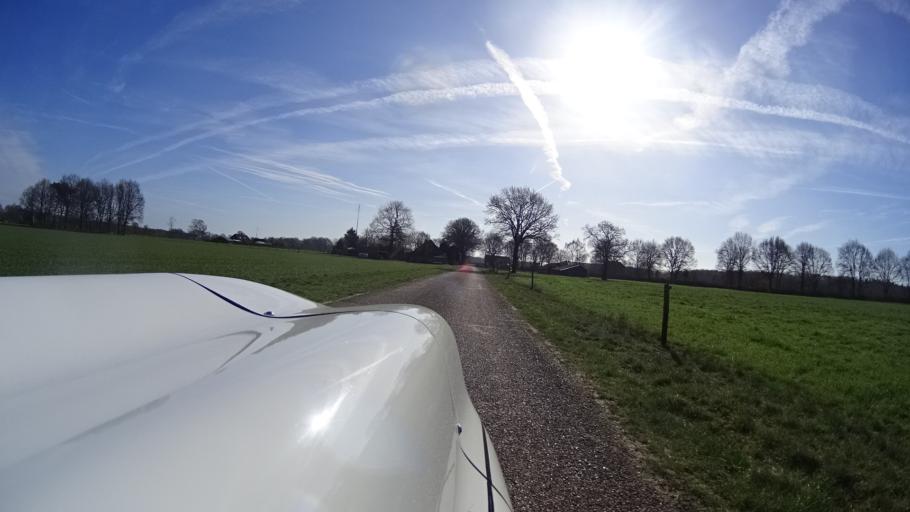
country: NL
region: North Brabant
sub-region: Gemeente Uden
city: Volkel
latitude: 51.6656
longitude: 5.6757
